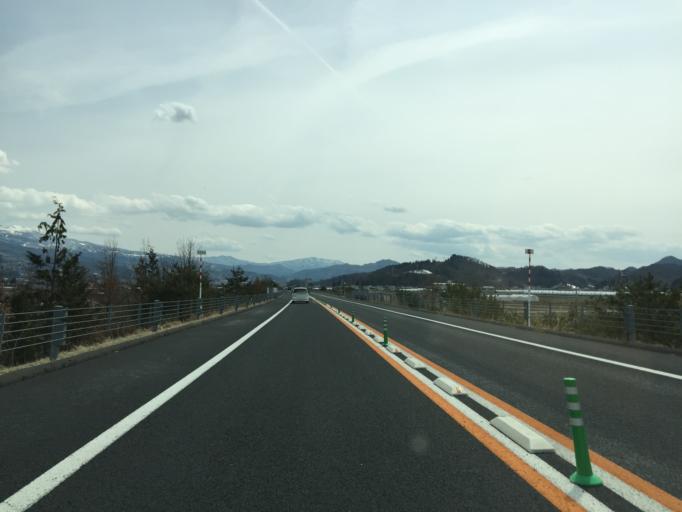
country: JP
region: Yamagata
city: Kaminoyama
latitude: 38.2279
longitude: 140.2773
